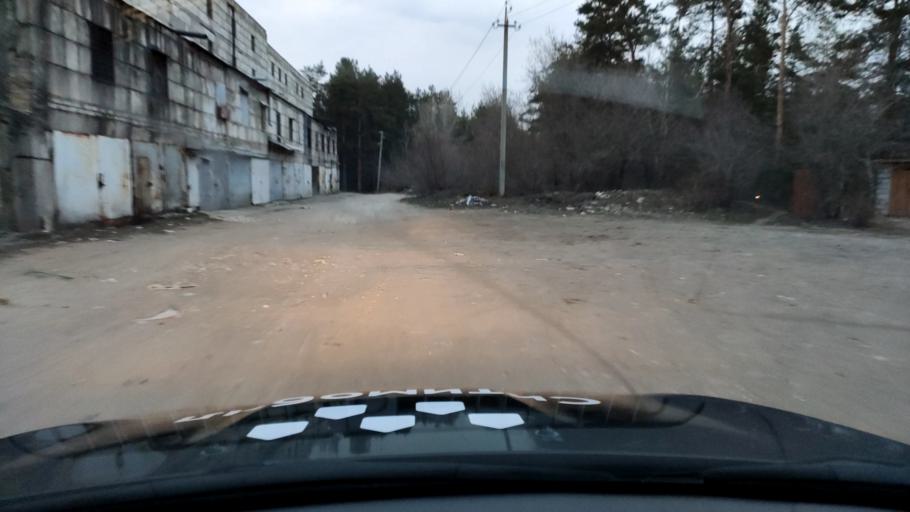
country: RU
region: Samara
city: Zhigulevsk
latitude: 53.4923
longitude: 49.4810
